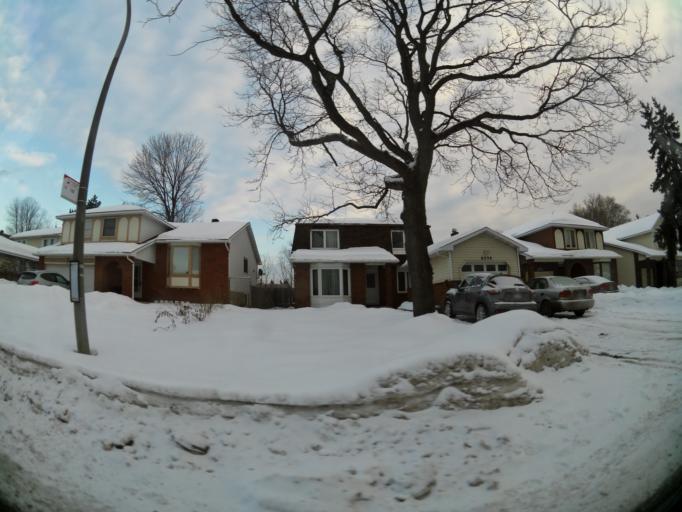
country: CA
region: Quebec
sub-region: Outaouais
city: Gatineau
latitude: 45.4716
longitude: -75.5418
